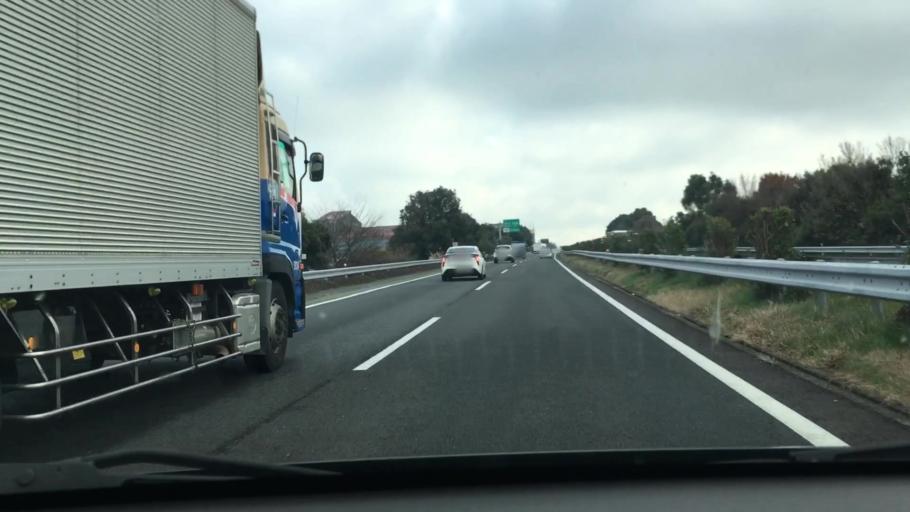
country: JP
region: Kumamoto
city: Kumamoto
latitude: 32.8420
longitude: 130.7739
